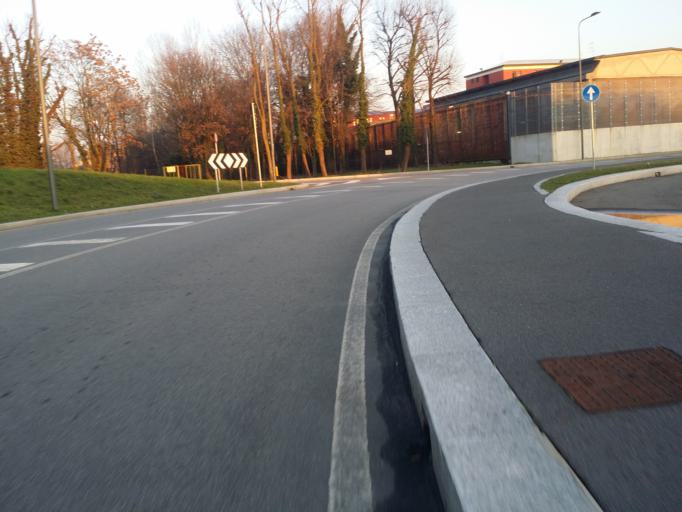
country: IT
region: Lombardy
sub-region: Citta metropolitana di Milano
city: Cesano Boscone
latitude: 45.4540
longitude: 9.1082
